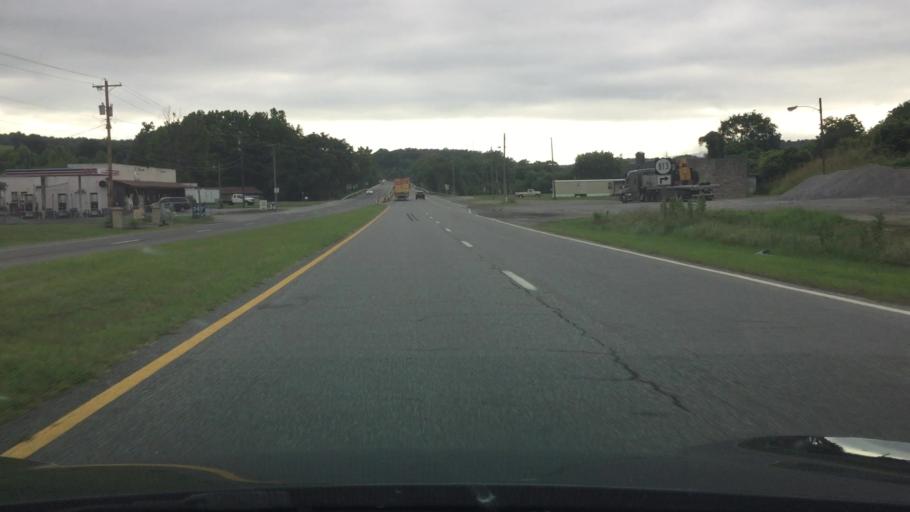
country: US
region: Virginia
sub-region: Montgomery County
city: Shawsville
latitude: 37.2325
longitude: -80.1964
